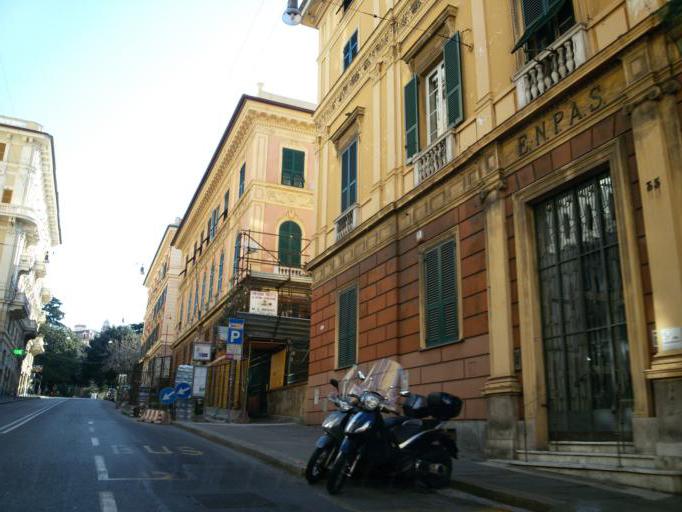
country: IT
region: Liguria
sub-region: Provincia di Genova
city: Genoa
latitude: 44.4132
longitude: 8.9452
